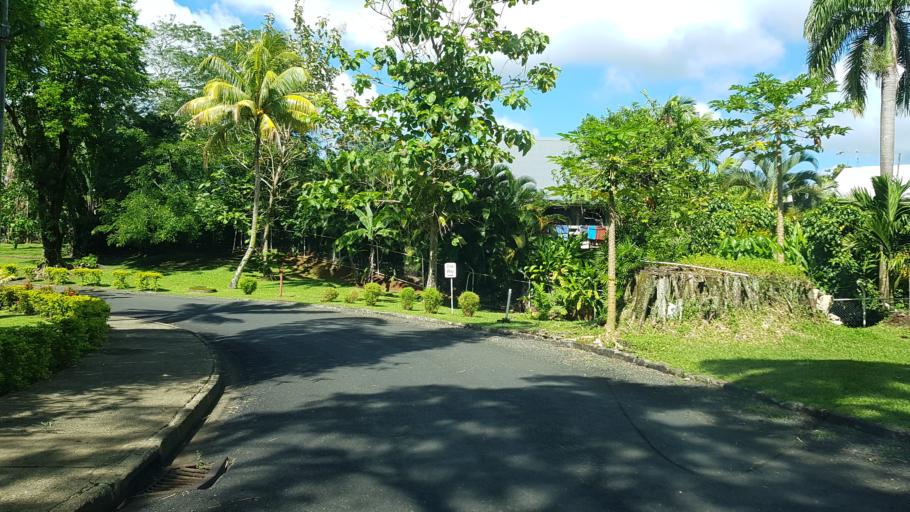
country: FJ
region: Central
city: Suva
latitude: -18.1440
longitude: 178.4561
